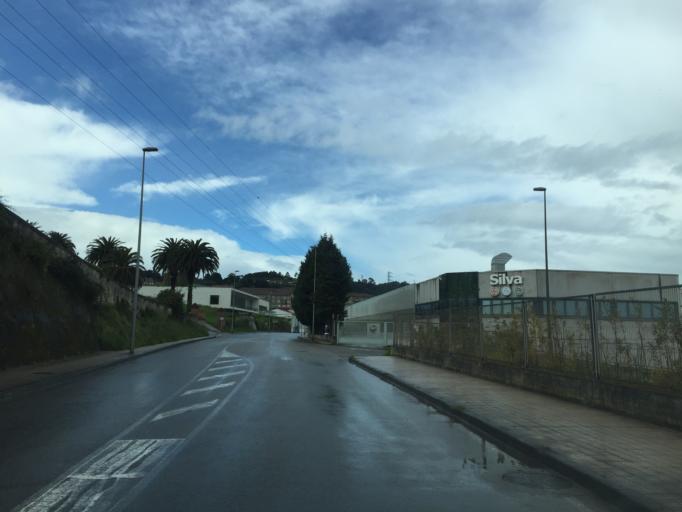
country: ES
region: Asturias
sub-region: Province of Asturias
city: Natahoyo
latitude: 43.5508
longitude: -5.6992
